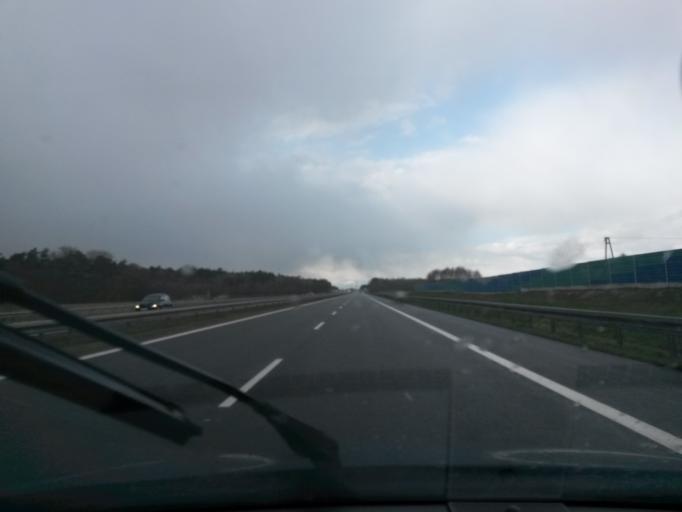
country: PL
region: Greater Poland Voivodeship
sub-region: Powiat koninski
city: Stare Miasto
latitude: 52.1749
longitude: 18.1448
